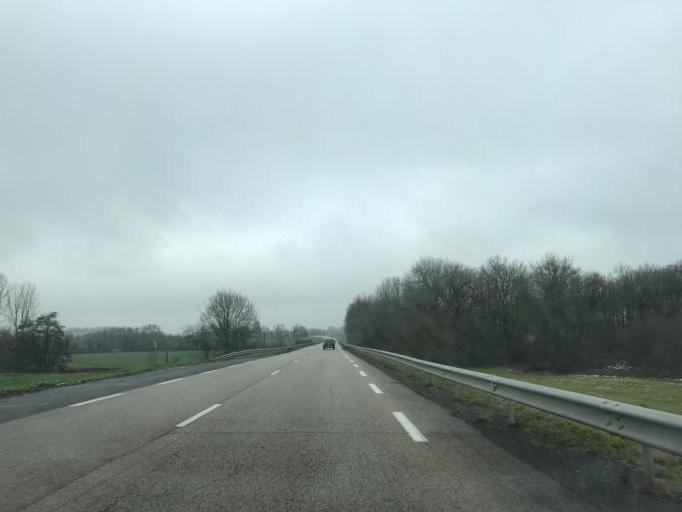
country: FR
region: Rhone-Alpes
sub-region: Departement de l'Ain
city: Saint-Paul-de-Varax
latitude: 46.0548
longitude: 5.0753
